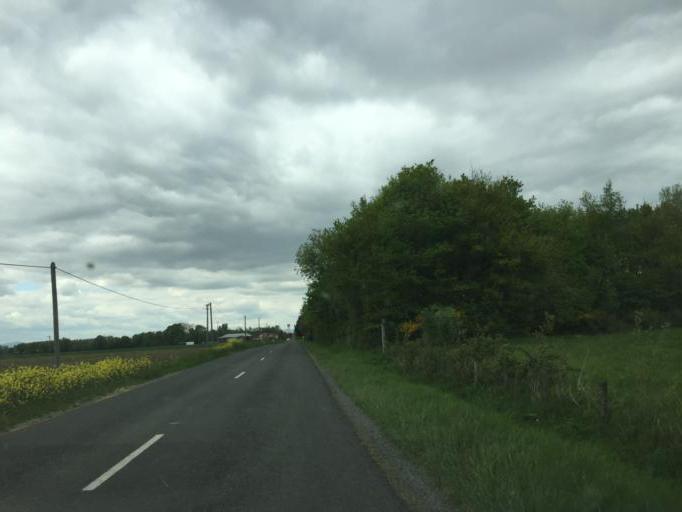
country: FR
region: Rhone-Alpes
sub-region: Departement de l'Ain
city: Amberieux-en-Dombes
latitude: 45.9780
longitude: 4.9263
